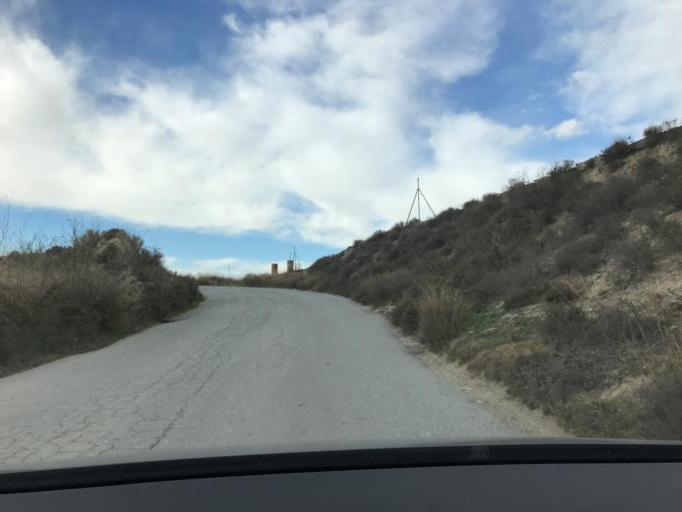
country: ES
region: Andalusia
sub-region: Provincia de Granada
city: Alhendin
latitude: 37.0973
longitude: -3.6571
